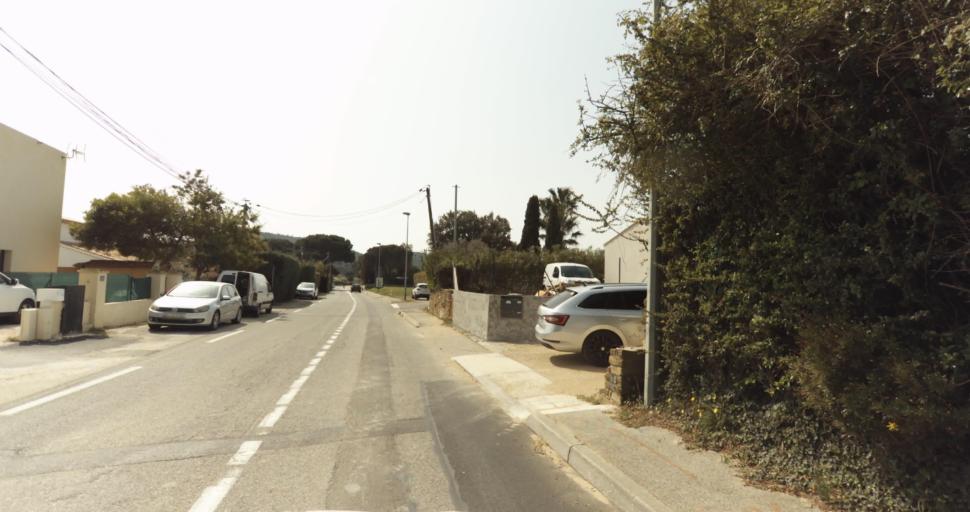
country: FR
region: Provence-Alpes-Cote d'Azur
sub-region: Departement du Var
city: Bormes-les-Mimosas
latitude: 43.1372
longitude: 6.3390
